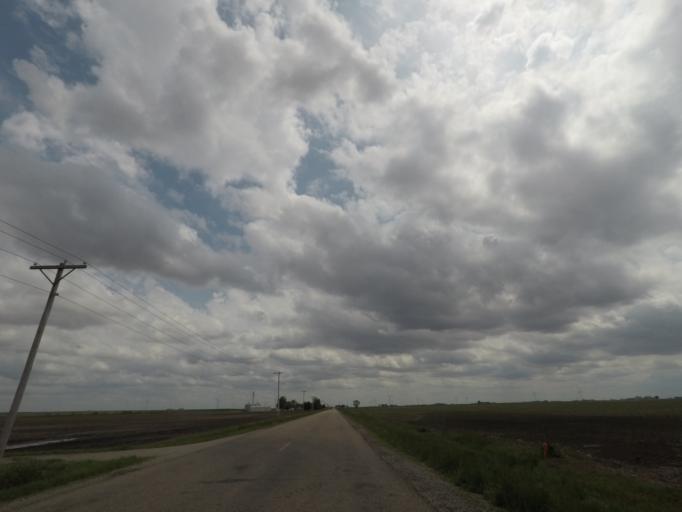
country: US
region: Illinois
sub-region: Macon County
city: Maroa
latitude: 40.0789
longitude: -89.0859
